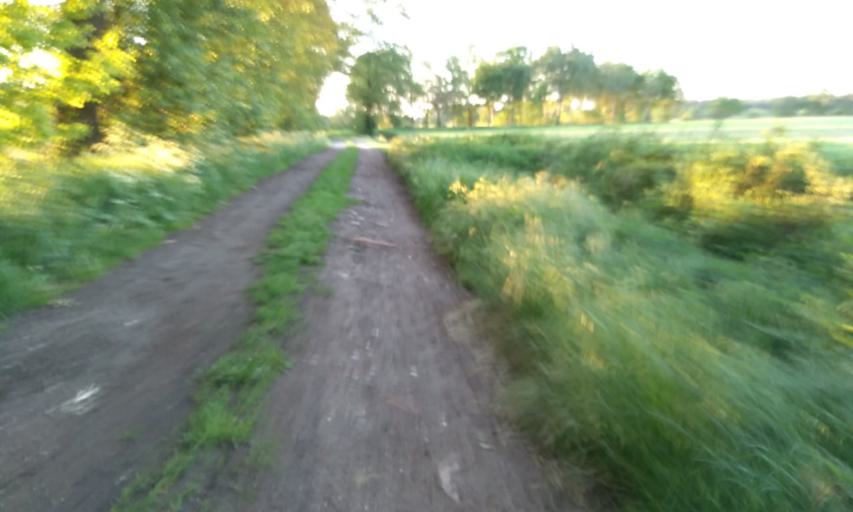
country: DE
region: Lower Saxony
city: Ahlerstedt
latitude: 53.4326
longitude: 9.4321
